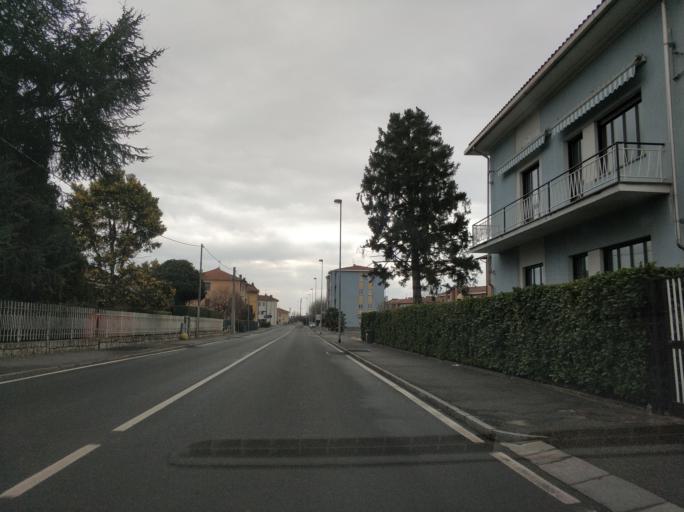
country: IT
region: Piedmont
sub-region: Provincia di Torino
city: Banchette
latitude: 45.4437
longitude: 7.8777
